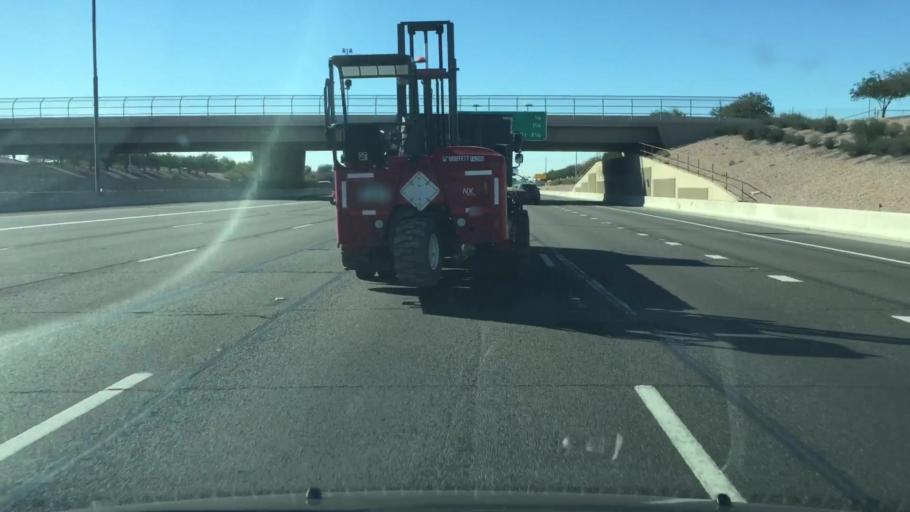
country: US
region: Arizona
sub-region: Maricopa County
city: Gilbert
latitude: 33.3847
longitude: -111.7955
